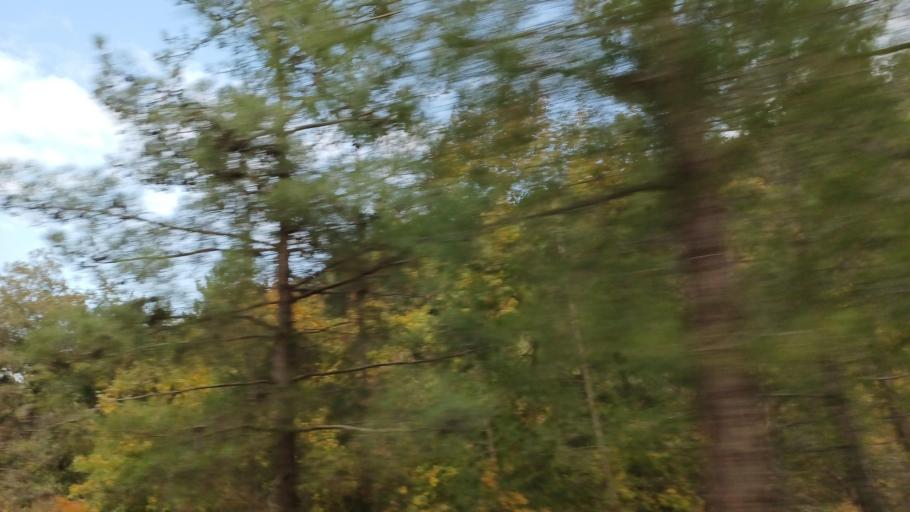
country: CY
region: Limassol
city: Pelendri
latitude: 34.9228
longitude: 32.9361
